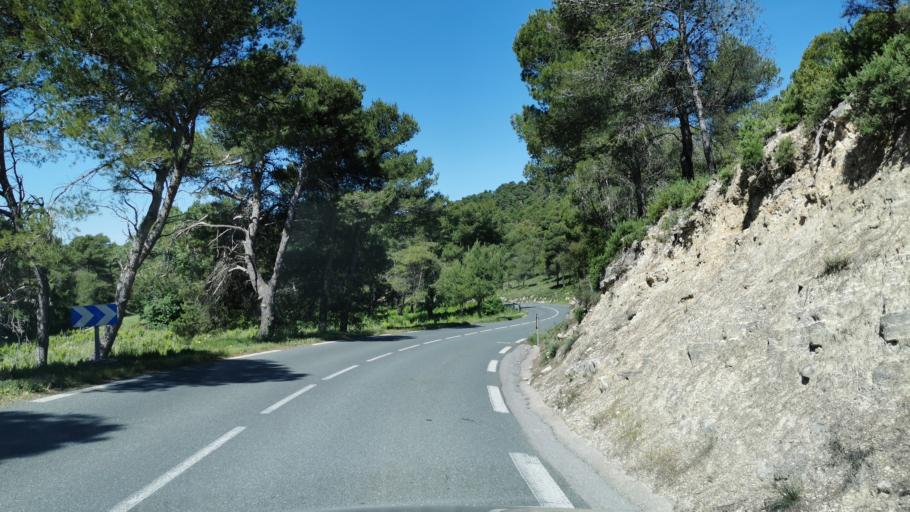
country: FR
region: Languedoc-Roussillon
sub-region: Departement de l'Aude
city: Armissan
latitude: 43.1747
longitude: 3.0830
